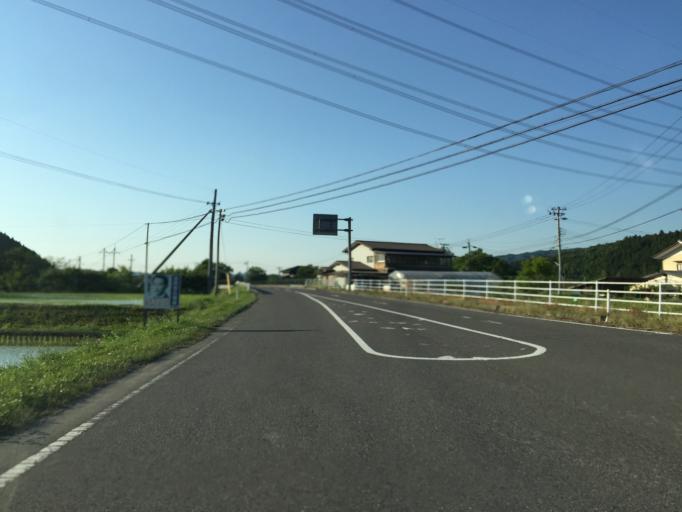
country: JP
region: Ibaraki
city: Daigo
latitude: 36.9456
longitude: 140.4403
